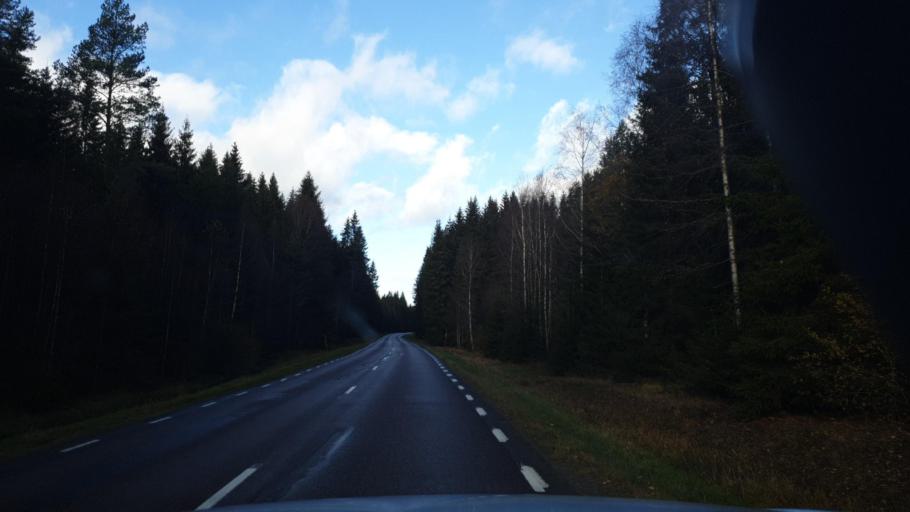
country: SE
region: Vaermland
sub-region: Grums Kommun
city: Slottsbron
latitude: 59.4572
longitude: 12.8371
